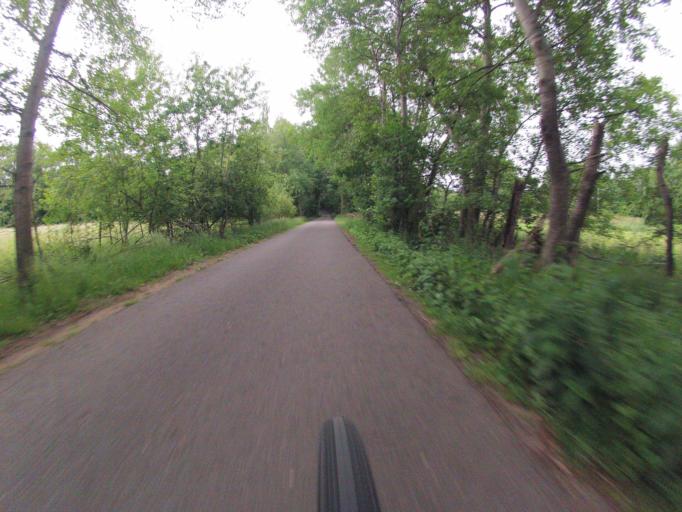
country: DE
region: North Rhine-Westphalia
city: Emsdetten
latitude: 52.2256
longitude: 7.5175
